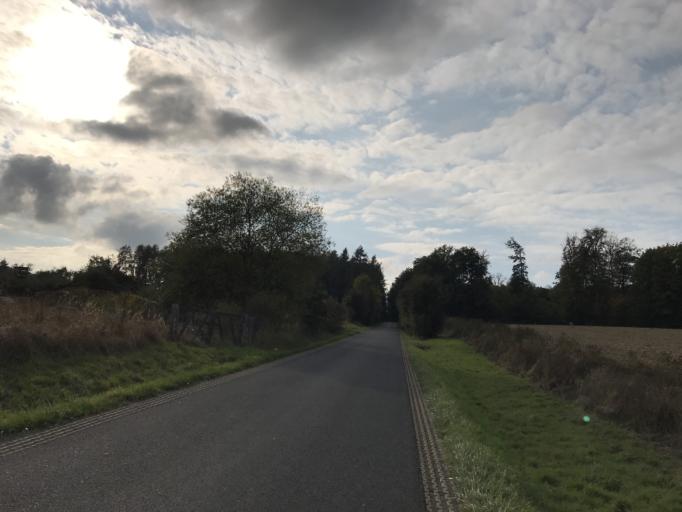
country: DE
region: Hesse
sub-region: Regierungsbezirk Giessen
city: Hoernsheim
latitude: 50.4935
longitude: 8.6318
